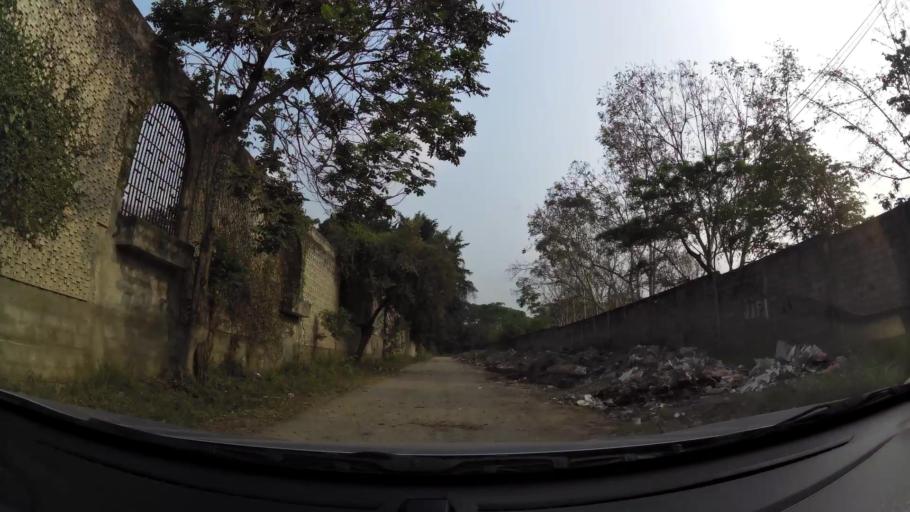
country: HN
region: Cortes
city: Armenta
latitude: 15.4846
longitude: -88.0408
